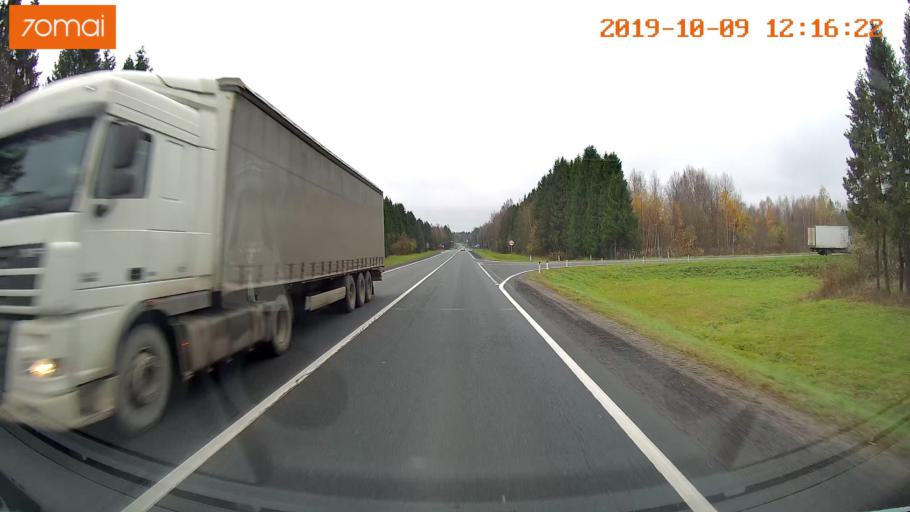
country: RU
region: Jaroslavl
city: Prechistoye
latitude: 58.4695
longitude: 40.3212
